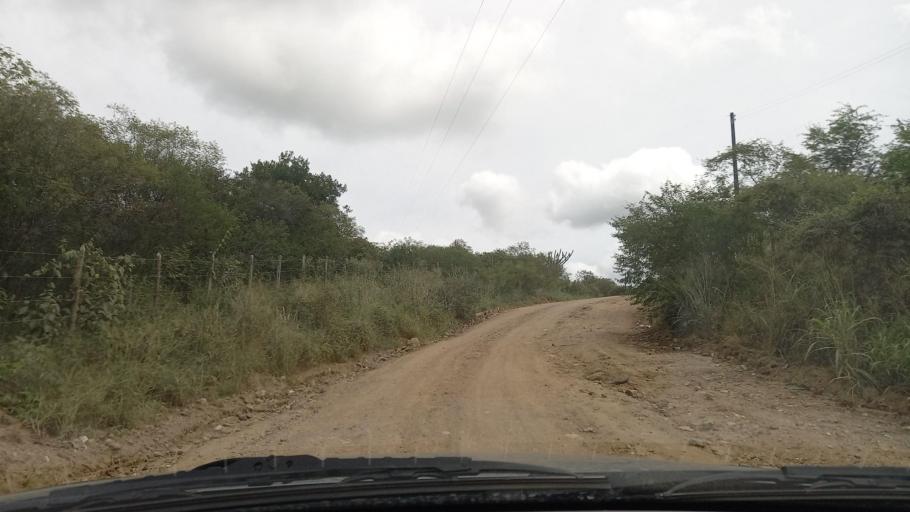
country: BR
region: Pernambuco
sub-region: Gravata
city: Gravata
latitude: -8.1819
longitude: -35.5885
